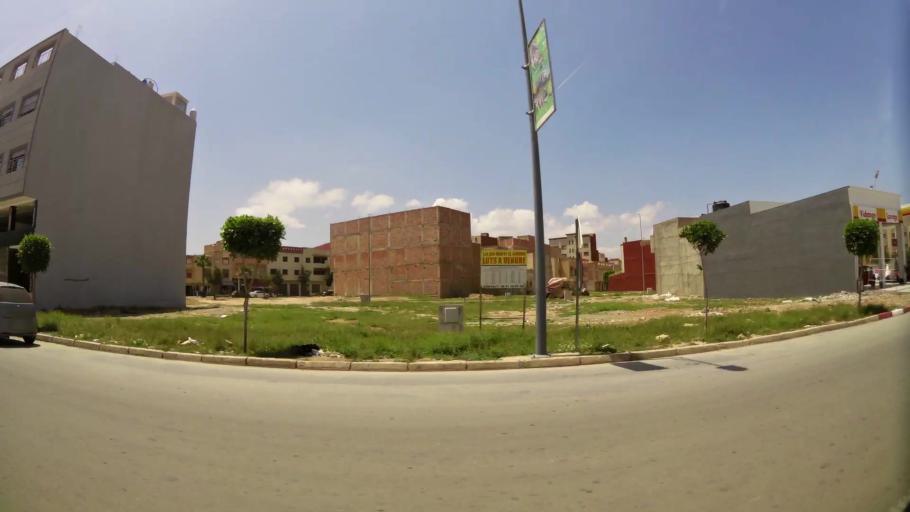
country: MA
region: Oriental
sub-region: Oujda-Angad
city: Oujda
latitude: 34.6908
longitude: -1.8918
